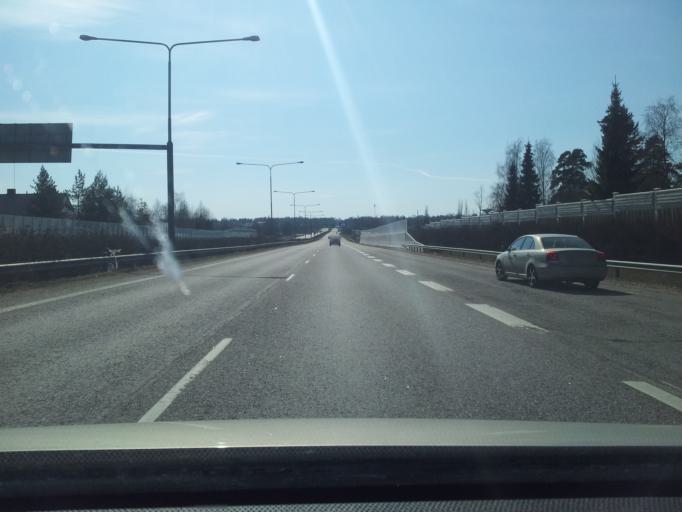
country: FI
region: Kymenlaakso
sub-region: Kotka-Hamina
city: Karhula
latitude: 60.5289
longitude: 26.9567
